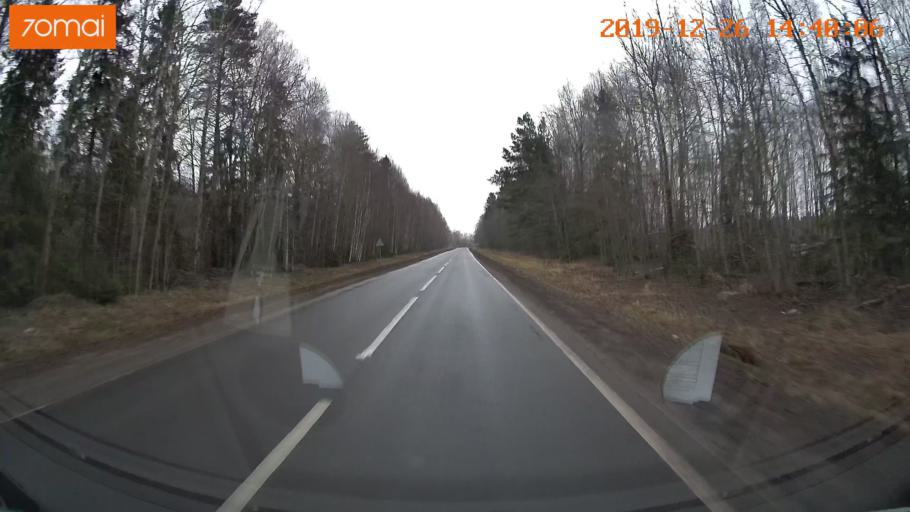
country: RU
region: Jaroslavl
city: Poshekhon'ye
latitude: 58.3780
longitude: 38.9916
